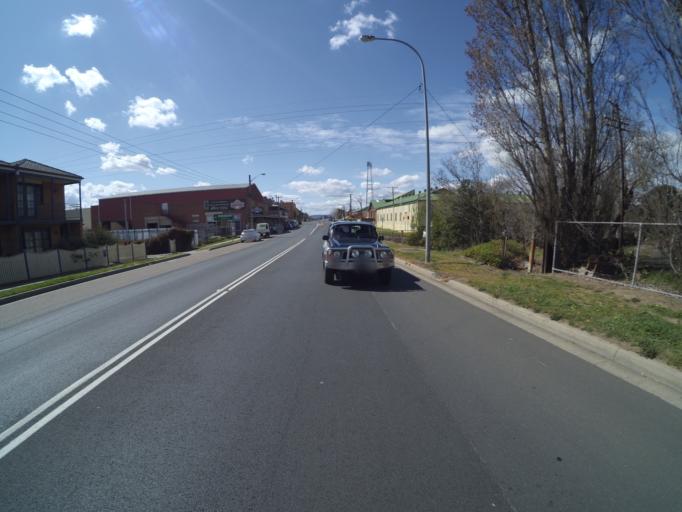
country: AU
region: New South Wales
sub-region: Goulburn Mulwaree
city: Goulburn
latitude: -34.7601
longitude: 149.7169
